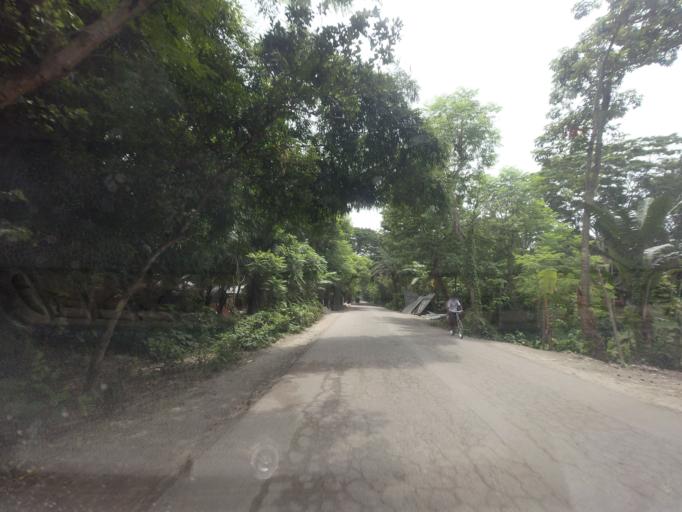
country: BD
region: Khulna
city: Kalia
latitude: 23.2083
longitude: 89.7032
